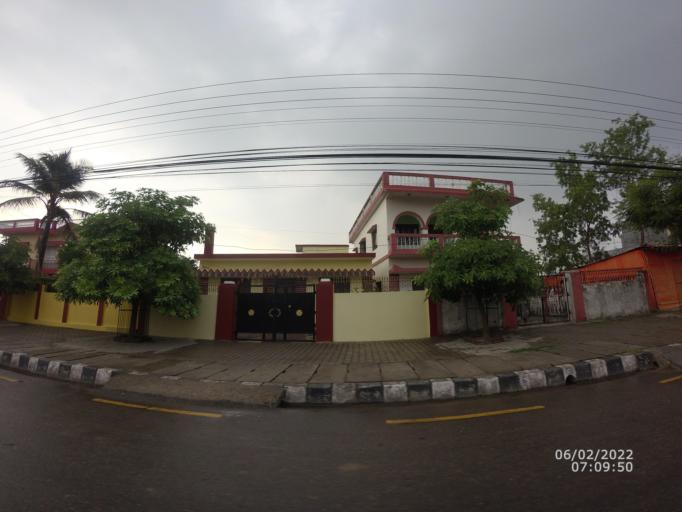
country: NP
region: Western Region
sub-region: Lumbini Zone
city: Bhairahawa
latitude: 27.4929
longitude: 83.4455
